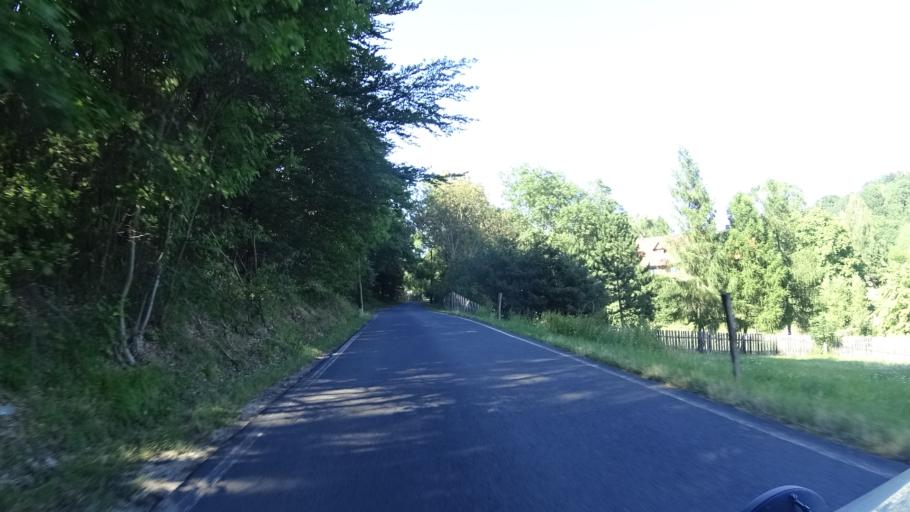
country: CZ
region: Ustecky
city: Zitenice
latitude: 50.5781
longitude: 14.1271
